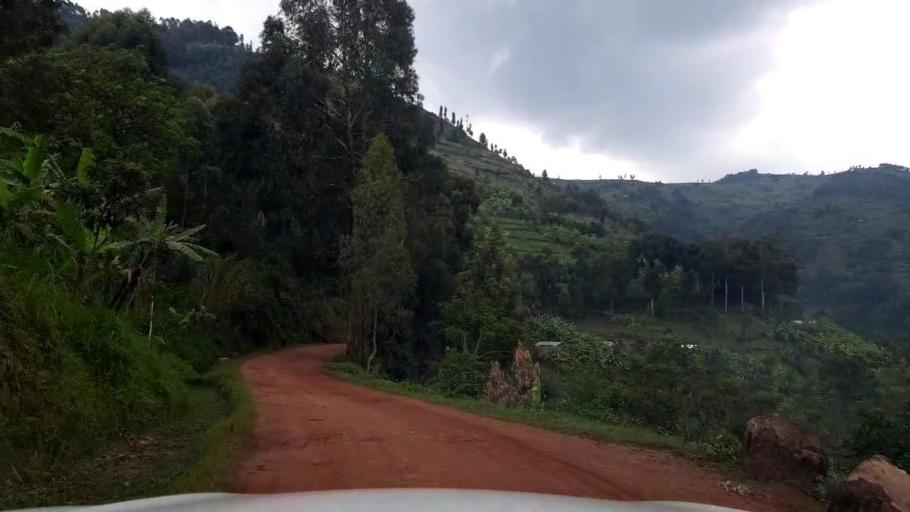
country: UG
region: Western Region
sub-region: Kisoro District
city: Kisoro
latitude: -1.3923
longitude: 29.7975
